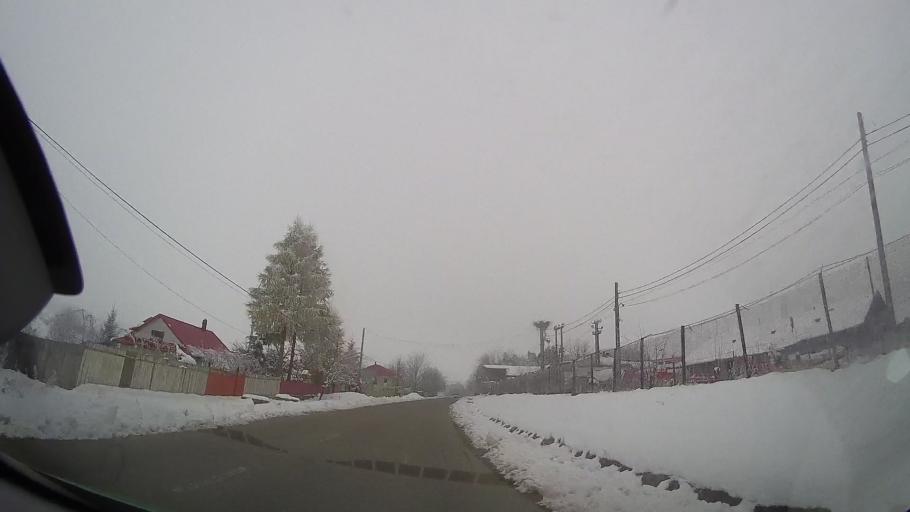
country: RO
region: Neamt
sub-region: Comuna Icusesti
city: Balusesti
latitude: 46.8574
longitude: 27.0251
